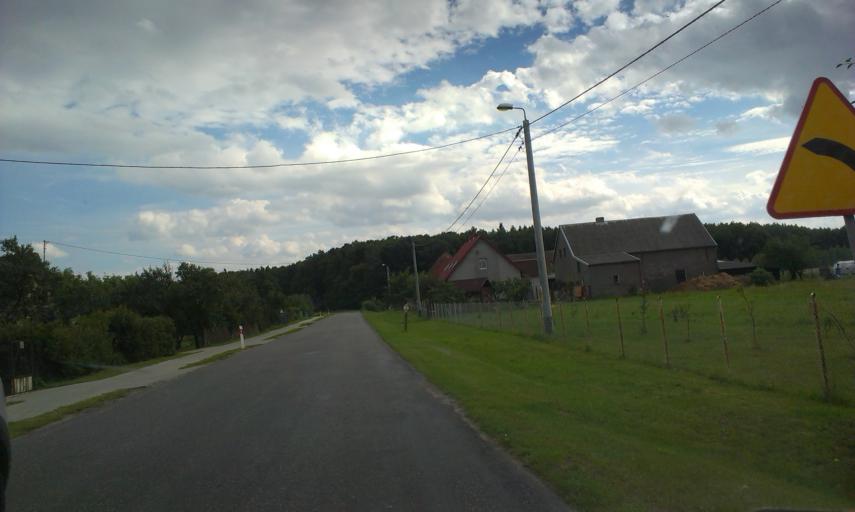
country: PL
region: Greater Poland Voivodeship
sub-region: Powiat zlotowski
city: Zlotow
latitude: 53.4170
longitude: 16.9863
